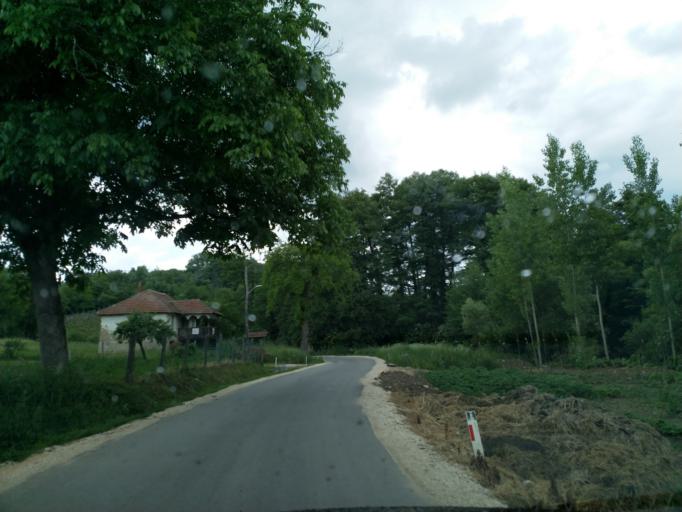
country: RS
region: Central Serbia
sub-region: Borski Okrug
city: Bor
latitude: 44.0202
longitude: 21.9798
